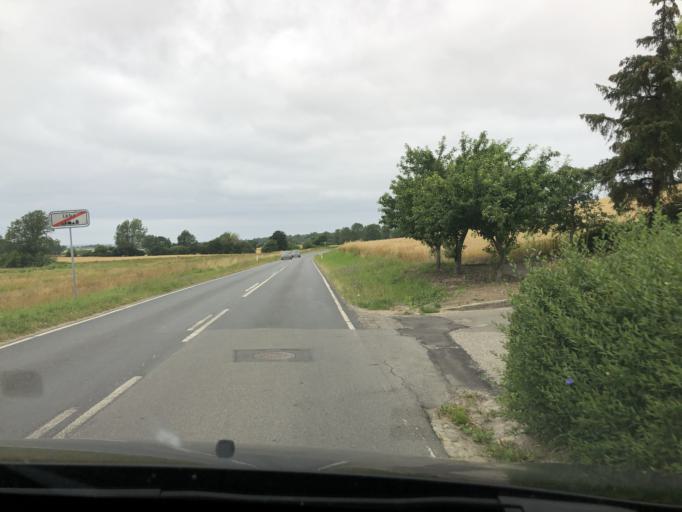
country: DK
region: South Denmark
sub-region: AEro Kommune
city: AEroskobing
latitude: 54.9151
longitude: 10.2830
